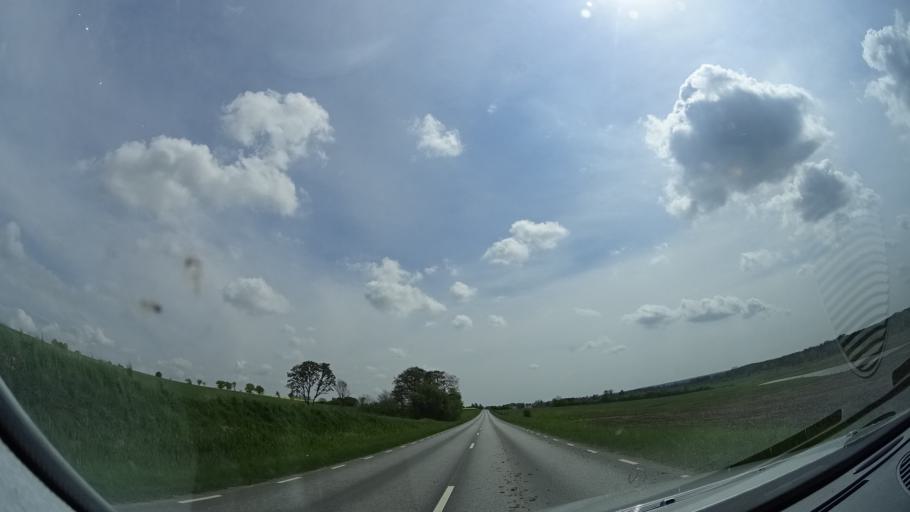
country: SE
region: Skane
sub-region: Hoors Kommun
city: Loberod
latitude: 55.7239
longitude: 13.5051
